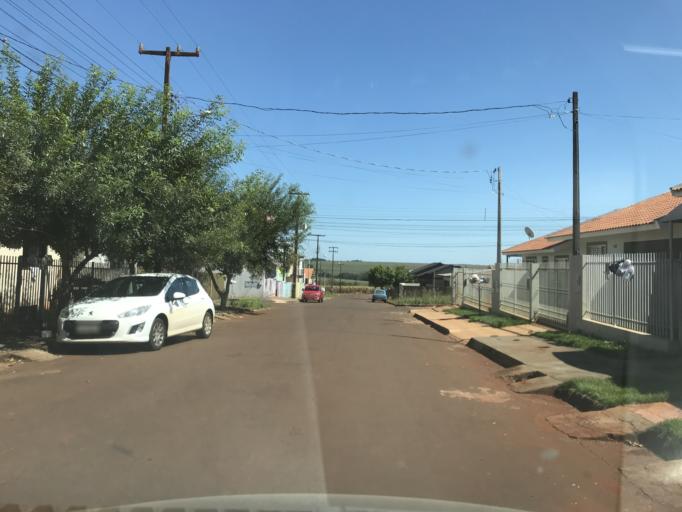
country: BR
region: Parana
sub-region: Palotina
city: Palotina
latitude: -24.3002
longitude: -53.8403
